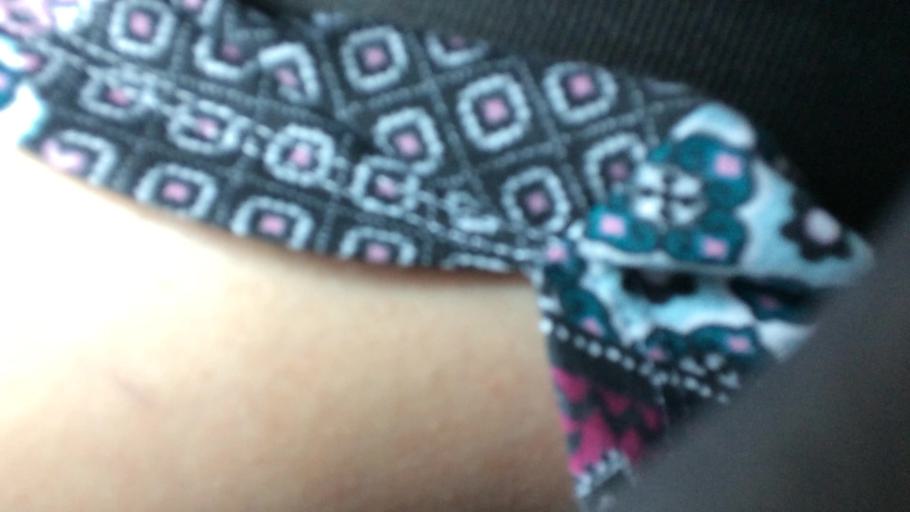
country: US
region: New Mexico
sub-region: Colfax County
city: Springer
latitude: 36.0683
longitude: -104.6902
